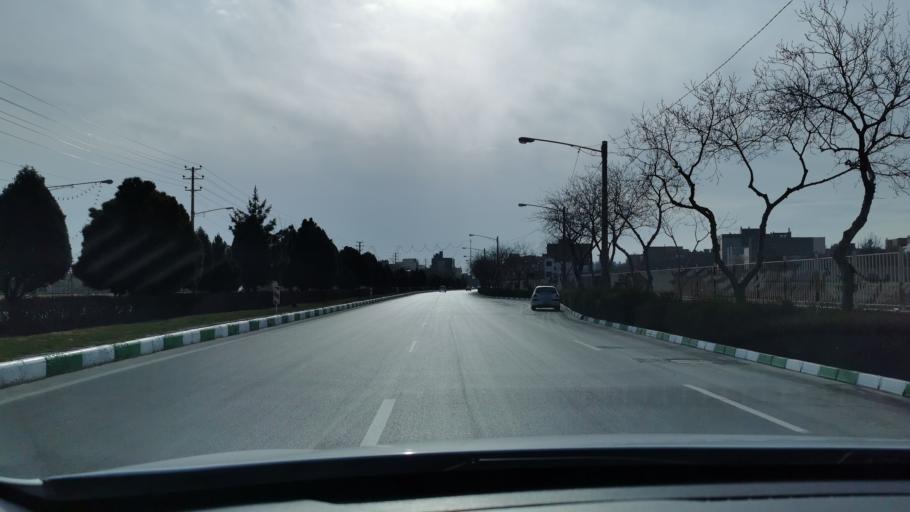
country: IR
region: Razavi Khorasan
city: Mashhad
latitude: 36.3005
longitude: 59.5212
